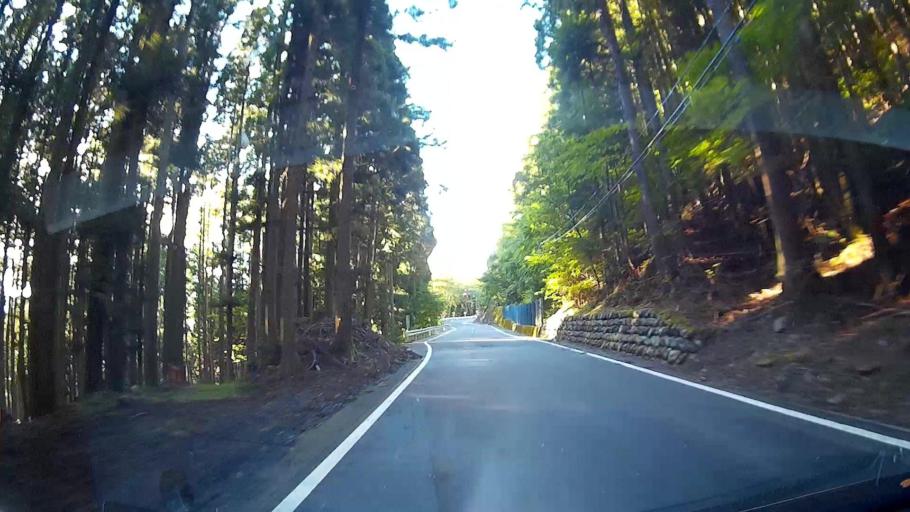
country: JP
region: Shizuoka
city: Shizuoka-shi
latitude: 35.2024
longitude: 138.2496
